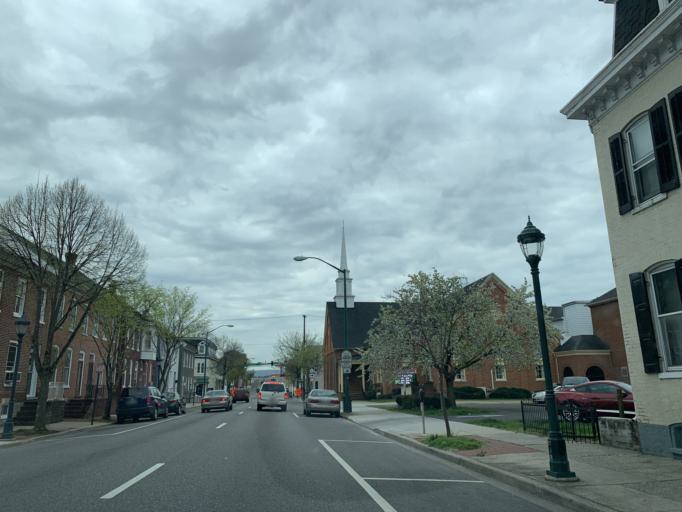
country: US
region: Maryland
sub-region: Washington County
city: Hagerstown
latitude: 39.6405
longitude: -77.7172
